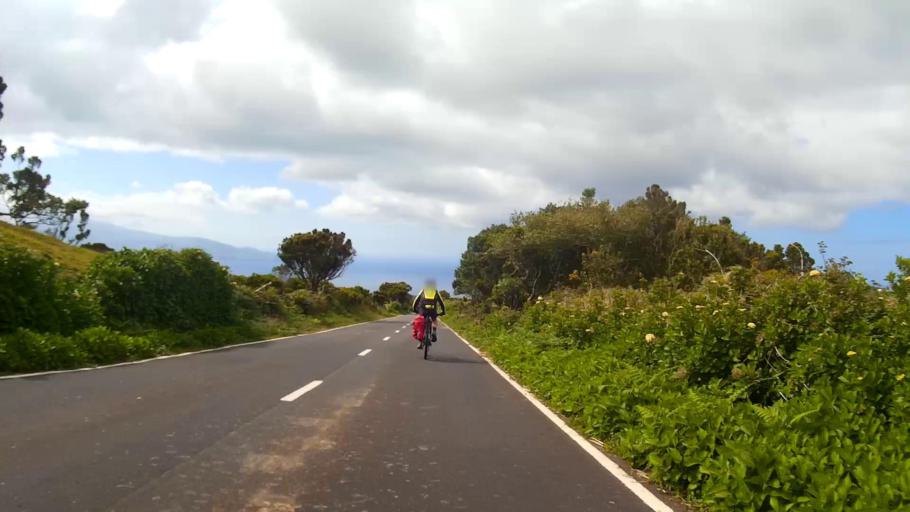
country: PT
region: Azores
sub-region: Madalena
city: Madalena
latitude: 38.4976
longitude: -28.4614
